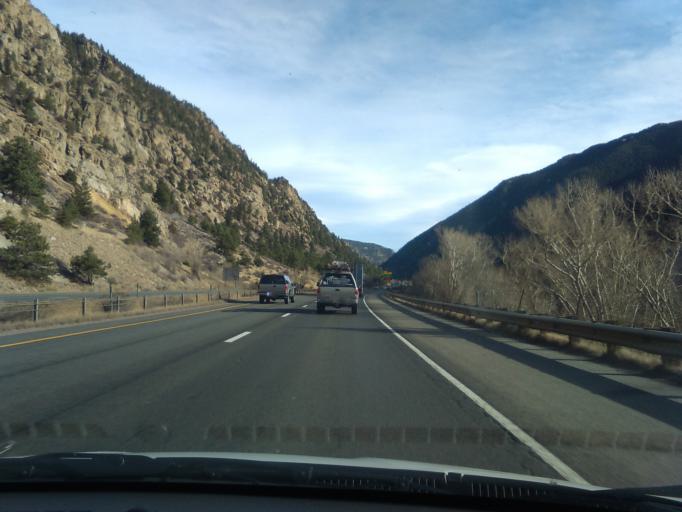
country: US
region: Colorado
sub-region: Clear Creek County
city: Georgetown
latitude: 39.7447
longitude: -105.6798
